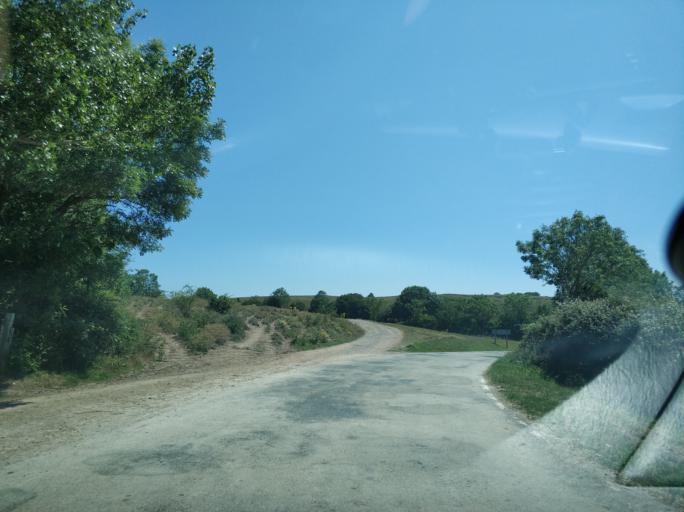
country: ES
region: Cantabria
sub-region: Provincia de Cantabria
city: Reinosa
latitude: 43.0148
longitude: -4.1629
